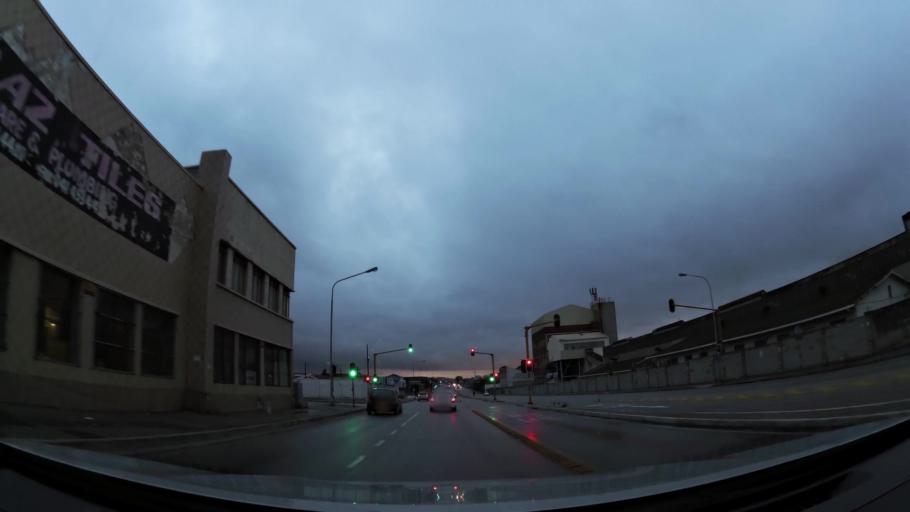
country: ZA
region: Eastern Cape
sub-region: Nelson Mandela Bay Metropolitan Municipality
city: Port Elizabeth
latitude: -33.9325
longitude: 25.5808
